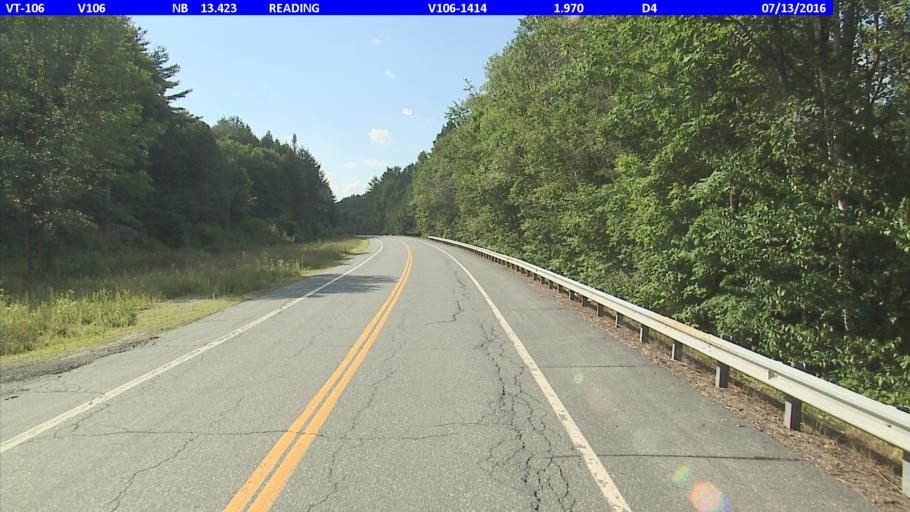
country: US
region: Vermont
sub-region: Windsor County
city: Windsor
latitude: 43.4718
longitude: -72.5345
